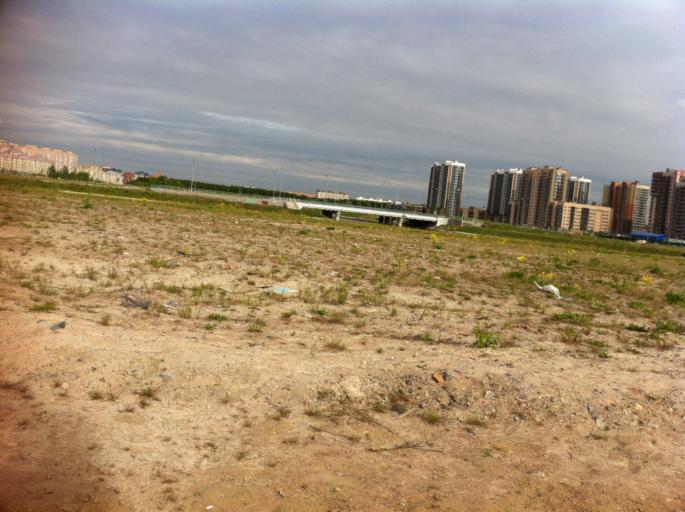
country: RU
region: St.-Petersburg
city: Sosnovaya Polyana
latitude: 59.8565
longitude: 30.1429
